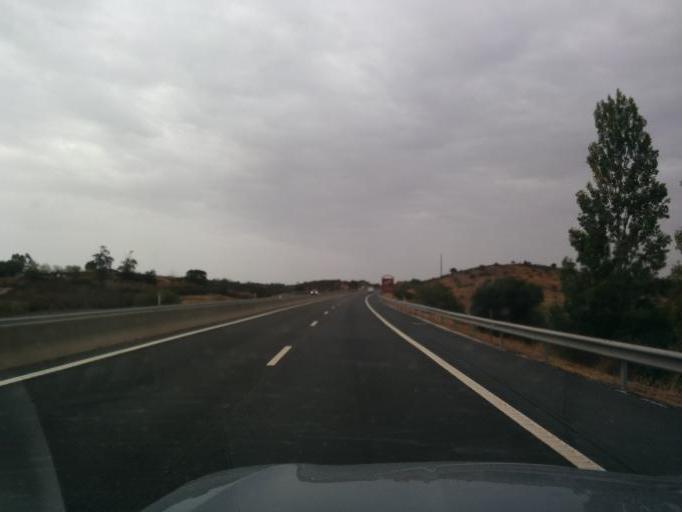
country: PT
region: Faro
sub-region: Castro Marim
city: Castro Marim
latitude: 37.2237
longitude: -7.4748
